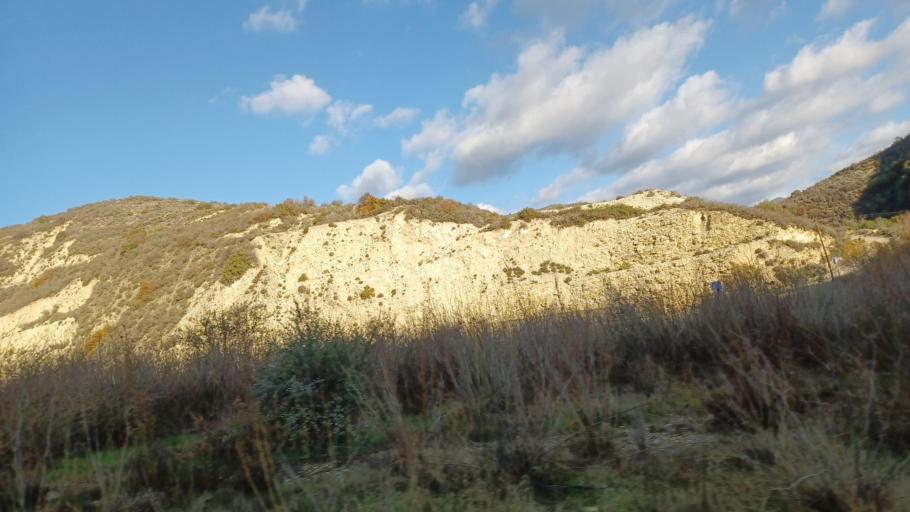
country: CY
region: Limassol
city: Pachna
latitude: 34.8571
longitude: 32.7302
